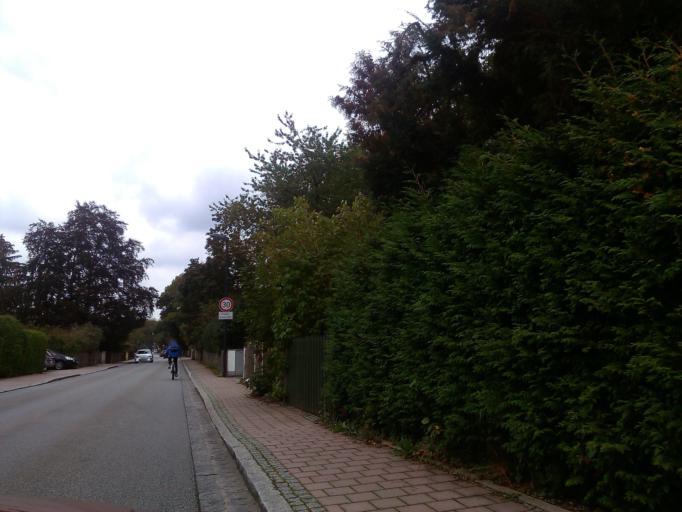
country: DE
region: Bavaria
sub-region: Upper Bavaria
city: Krailling
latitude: 48.0979
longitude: 11.4078
